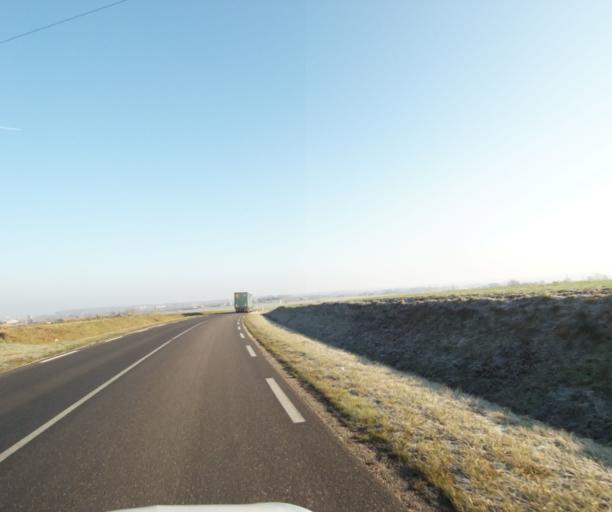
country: FR
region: Champagne-Ardenne
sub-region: Departement de la Haute-Marne
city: Montier-en-Der
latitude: 48.4590
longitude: 4.7504
